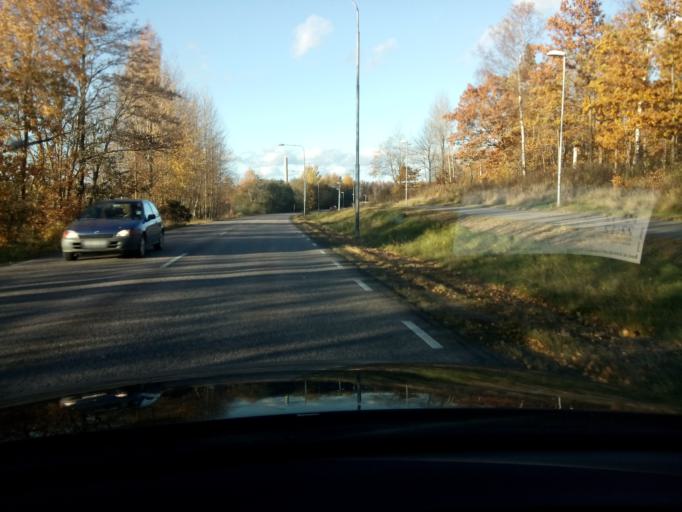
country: SE
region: Soedermanland
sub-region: Nykopings Kommun
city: Nykoping
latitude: 58.7343
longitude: 17.0063
